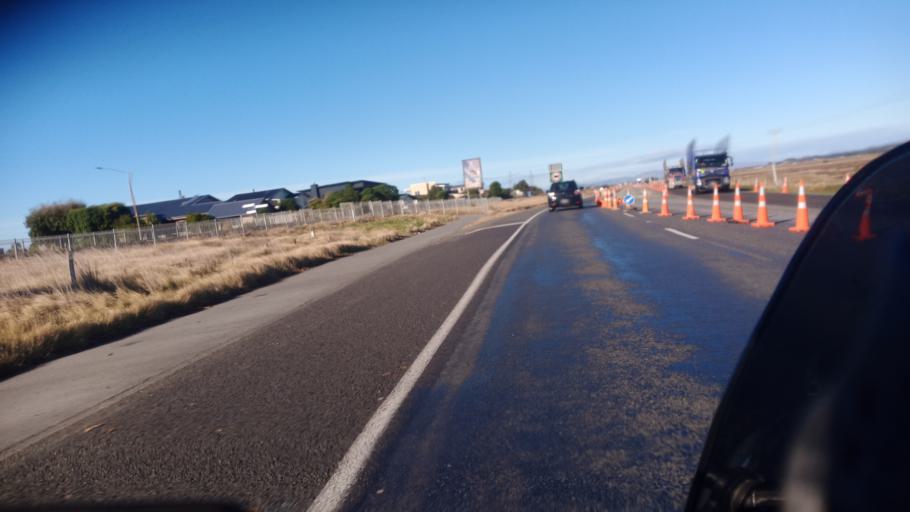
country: NZ
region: Hawke's Bay
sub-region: Napier City
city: Napier
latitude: -39.4412
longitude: 176.8710
